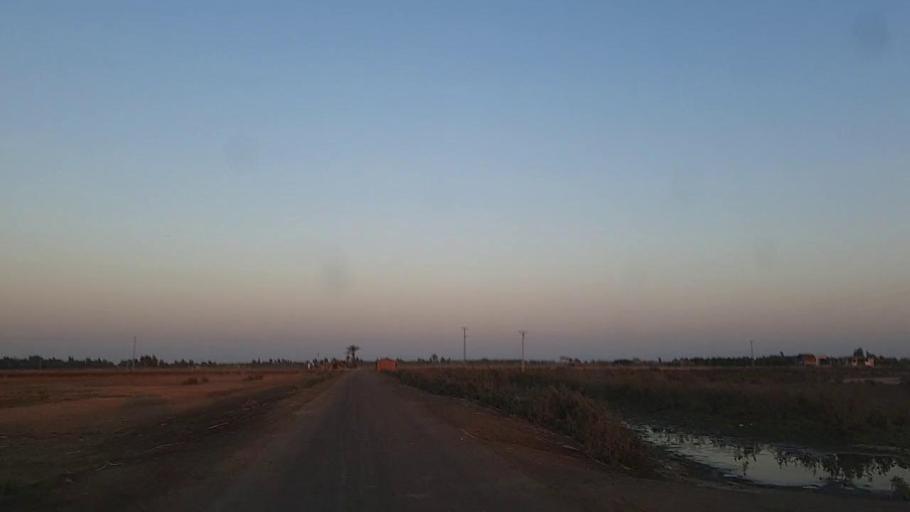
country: PK
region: Sindh
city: Samaro
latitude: 25.3092
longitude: 69.3880
